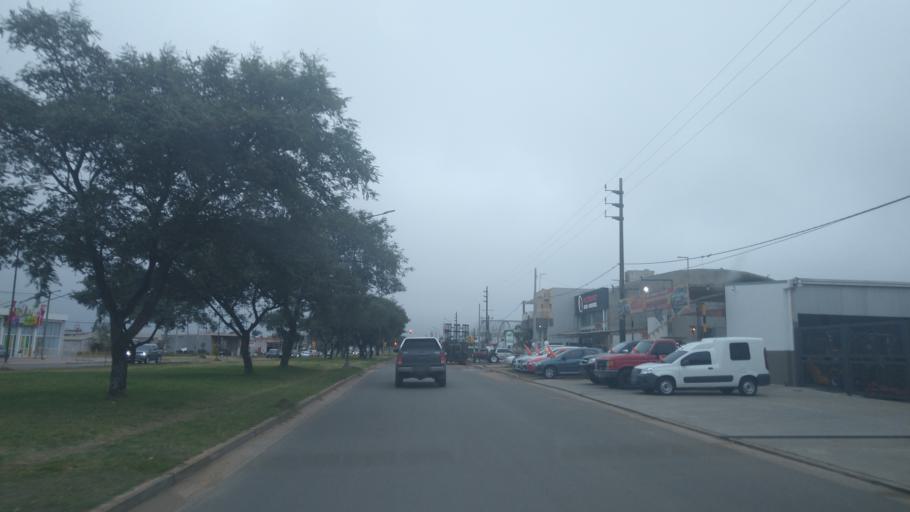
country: AR
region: Entre Rios
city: Chajari
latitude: -30.7611
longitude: -58.0047
